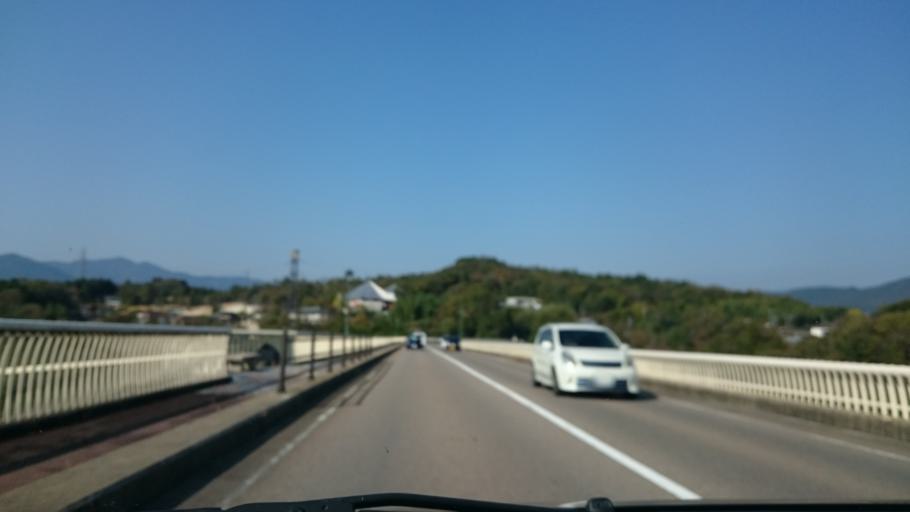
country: JP
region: Gifu
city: Nakatsugawa
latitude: 35.5087
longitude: 137.4747
